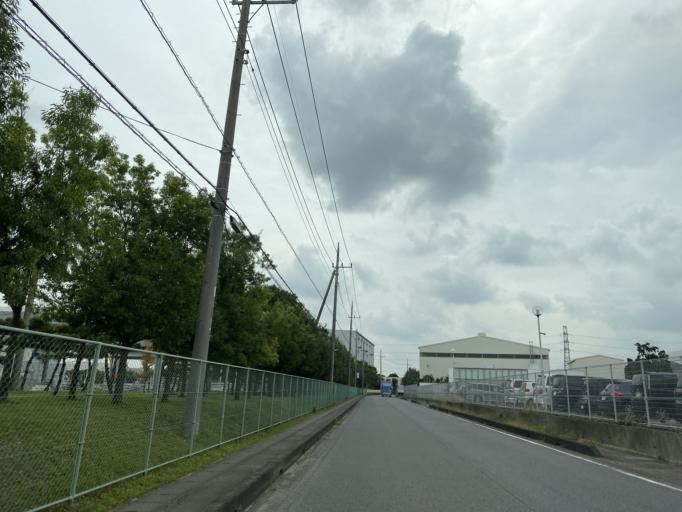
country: JP
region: Ibaraki
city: Mitsukaido
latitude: 36.0232
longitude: 140.0495
